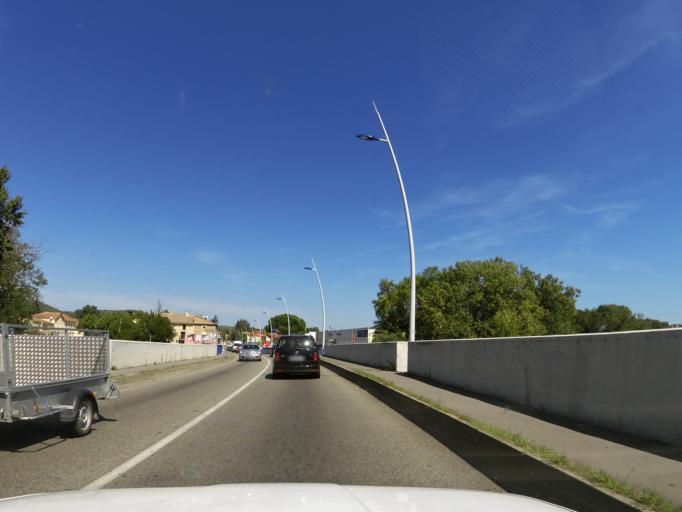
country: FR
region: Languedoc-Roussillon
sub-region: Departement du Gard
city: Bagnols-sur-Ceze
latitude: 44.1701
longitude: 4.6199
